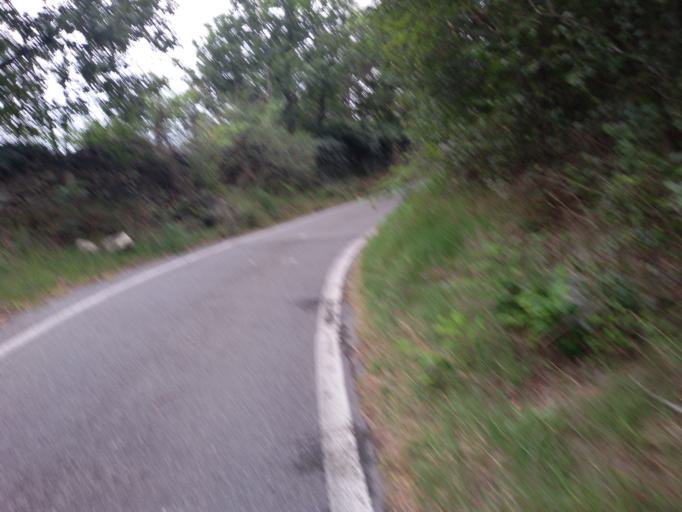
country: IT
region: Piedmont
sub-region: Provincia di Torino
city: Borgone Susa
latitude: 45.1264
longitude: 7.2338
